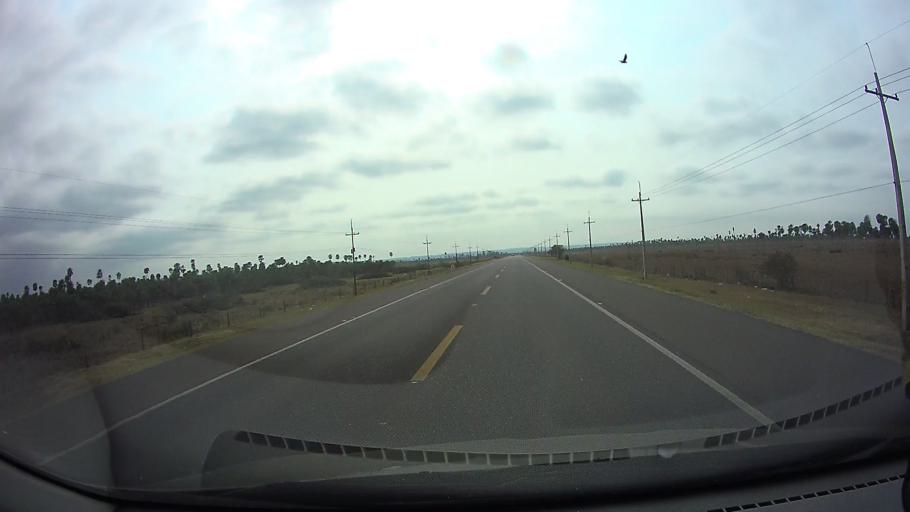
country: PY
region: Cordillera
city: Emboscada
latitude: -25.0785
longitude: -57.2713
